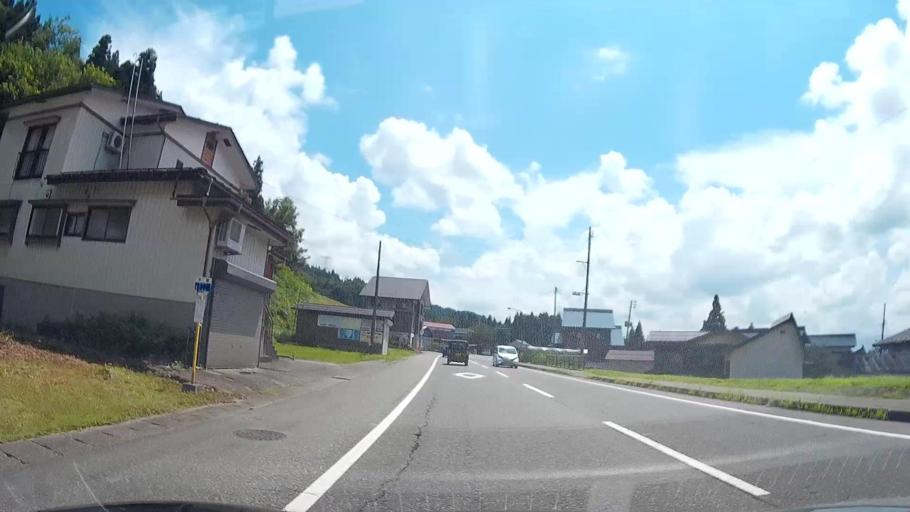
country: JP
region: Niigata
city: Tokamachi
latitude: 37.0853
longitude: 138.7227
